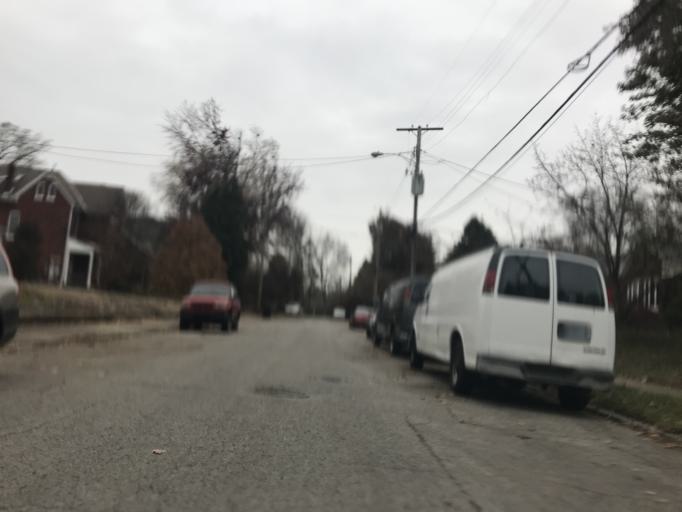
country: US
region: Indiana
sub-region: Clark County
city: Jeffersonville
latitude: 38.2568
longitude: -85.7070
